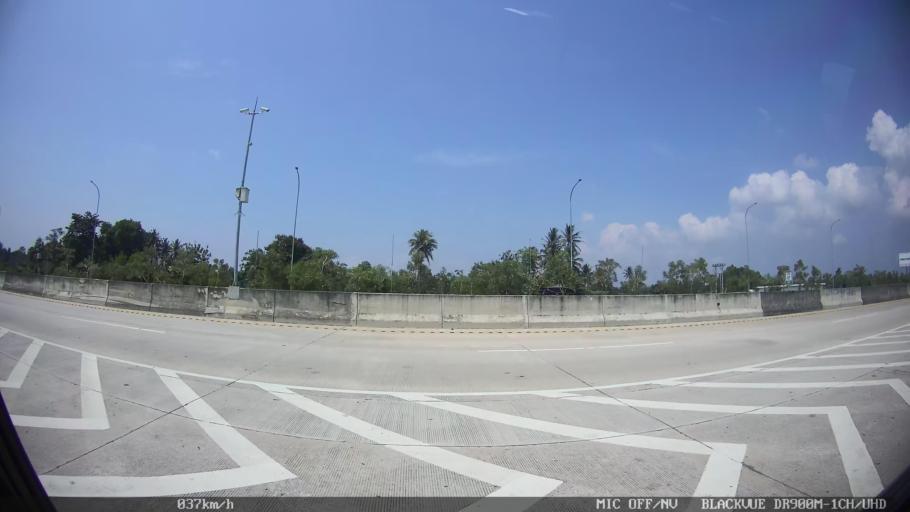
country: ID
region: Lampung
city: Kedaton
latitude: -5.3196
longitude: 105.2681
